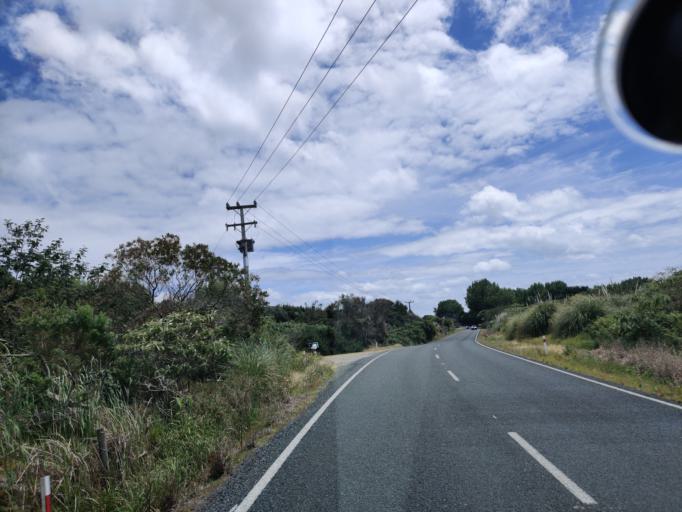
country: NZ
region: Northland
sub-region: Far North District
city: Kaitaia
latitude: -34.8799
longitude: 173.1546
